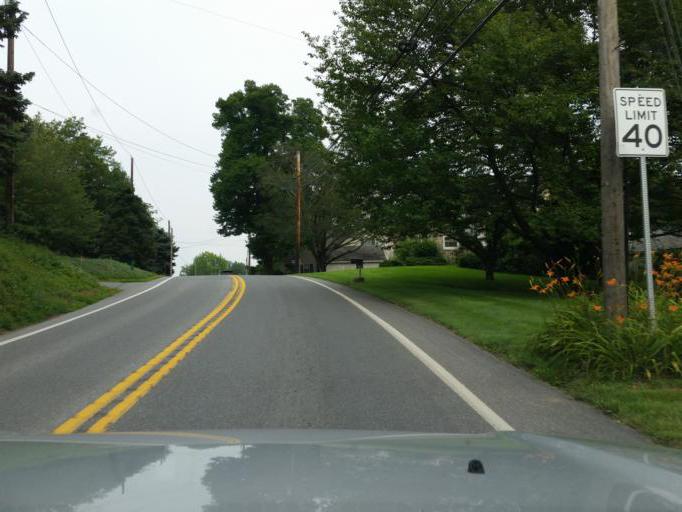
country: US
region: Pennsylvania
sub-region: Lancaster County
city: Manheim
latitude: 40.1533
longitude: -76.3728
